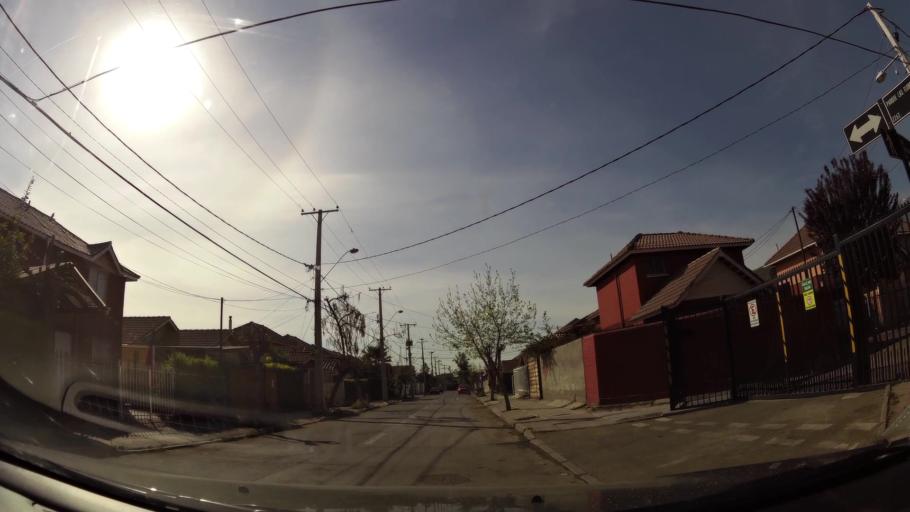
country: CL
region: Santiago Metropolitan
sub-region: Provincia de Cordillera
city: Puente Alto
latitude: -33.5891
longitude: -70.5526
